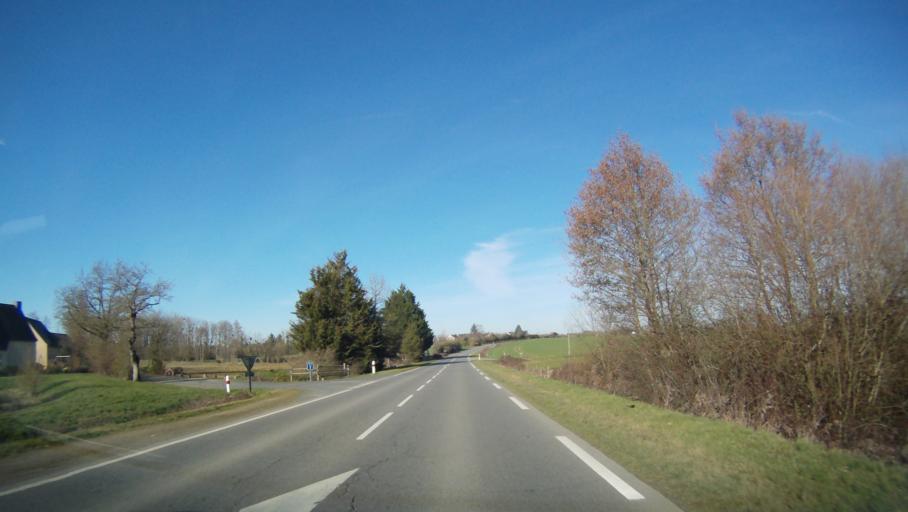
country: FR
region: Brittany
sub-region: Departement d'Ille-et-Vilaine
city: Bourgbarre
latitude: 47.9983
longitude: -1.6242
